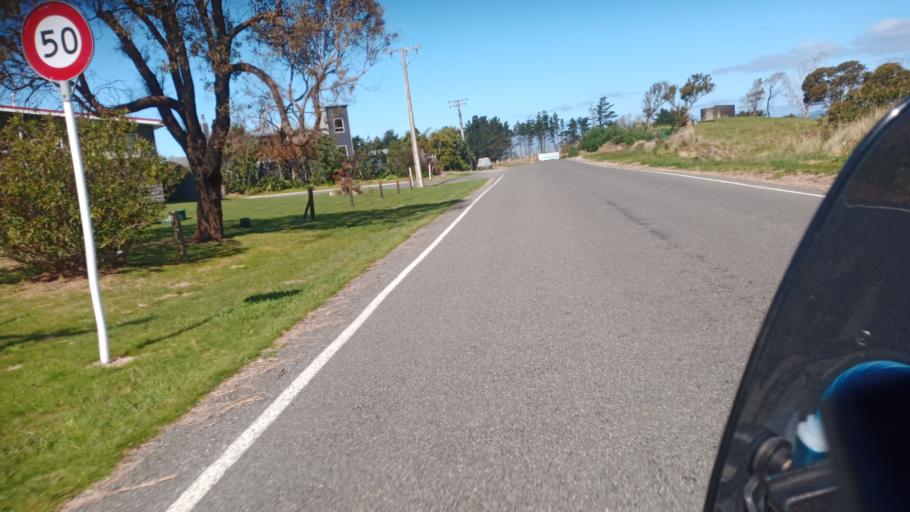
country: NZ
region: Gisborne
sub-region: Gisborne District
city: Gisborne
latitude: -39.0172
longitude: 177.8818
